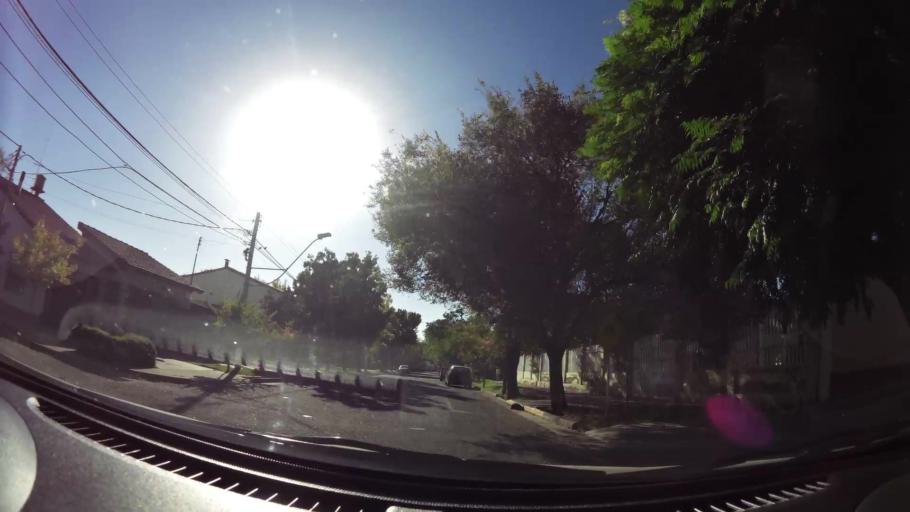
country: AR
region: Mendoza
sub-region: Departamento de Godoy Cruz
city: Godoy Cruz
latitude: -32.9382
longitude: -68.8362
